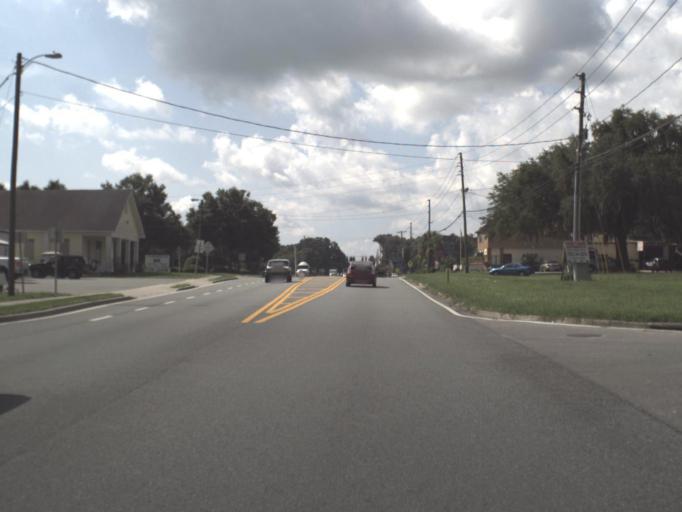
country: US
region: Florida
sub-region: Citrus County
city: Hernando
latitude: 28.9008
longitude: -82.3750
